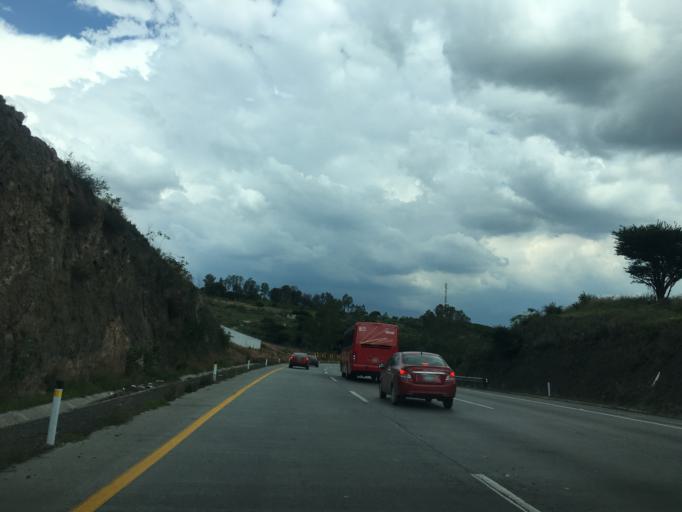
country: MX
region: Hidalgo
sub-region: Tepeji del Rio de Ocampo
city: Santiago Tlautla
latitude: 19.9699
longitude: -99.4307
